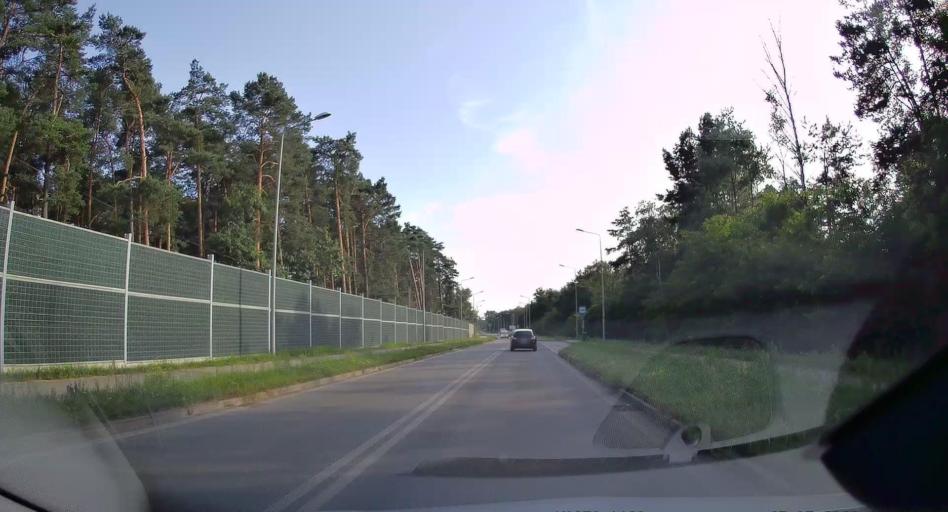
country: PL
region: Swietokrzyskie
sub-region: Powiat konecki
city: Konskie
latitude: 51.1211
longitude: 20.3539
